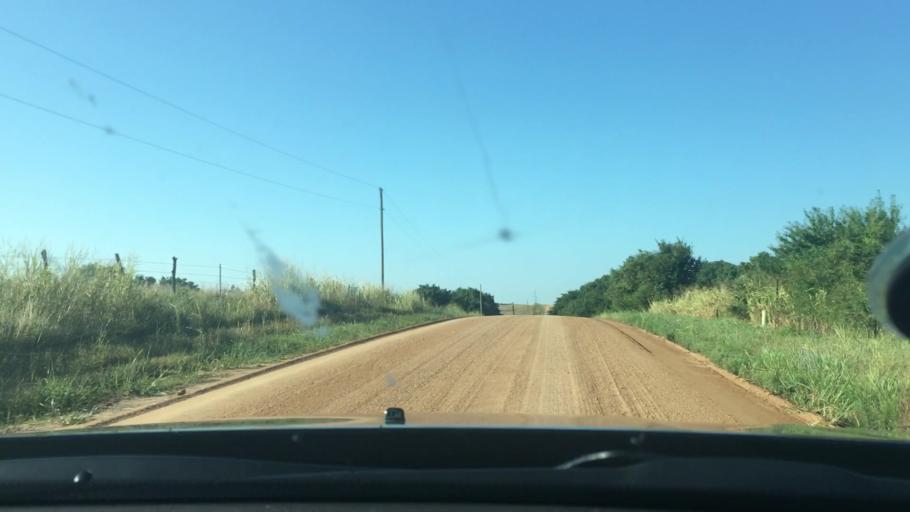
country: US
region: Oklahoma
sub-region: Murray County
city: Sulphur
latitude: 34.4143
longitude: -96.7936
